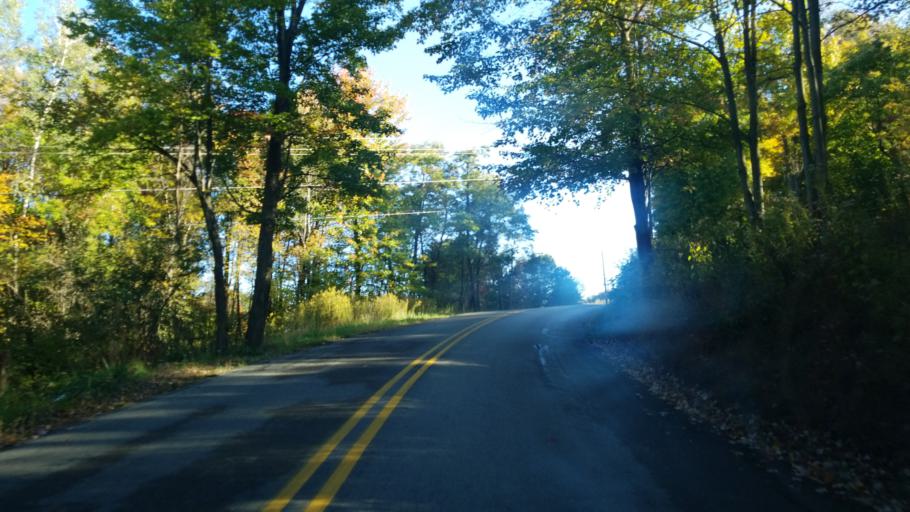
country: US
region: Pennsylvania
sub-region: Indiana County
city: Johnsonburg
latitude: 40.9066
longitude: -78.8774
